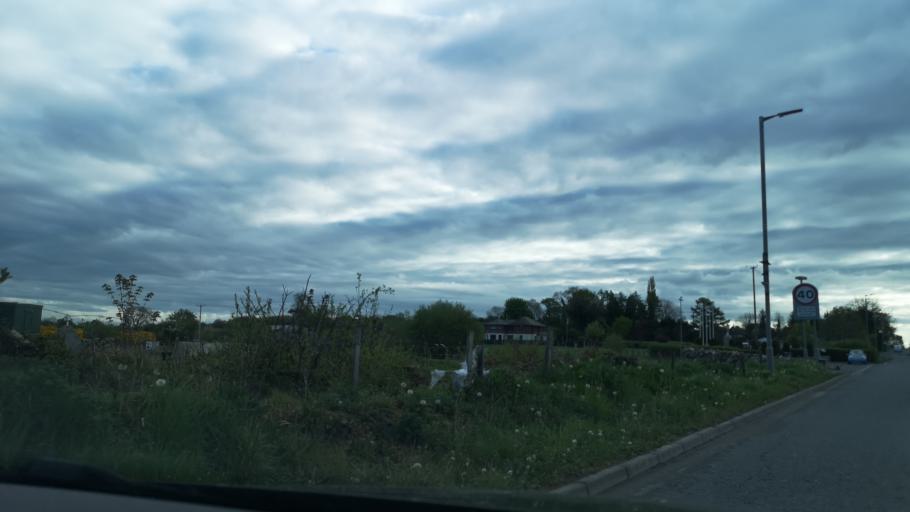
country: GB
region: Northern Ireland
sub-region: Newry and Mourne District
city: Newry
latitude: 54.1818
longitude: -6.4057
